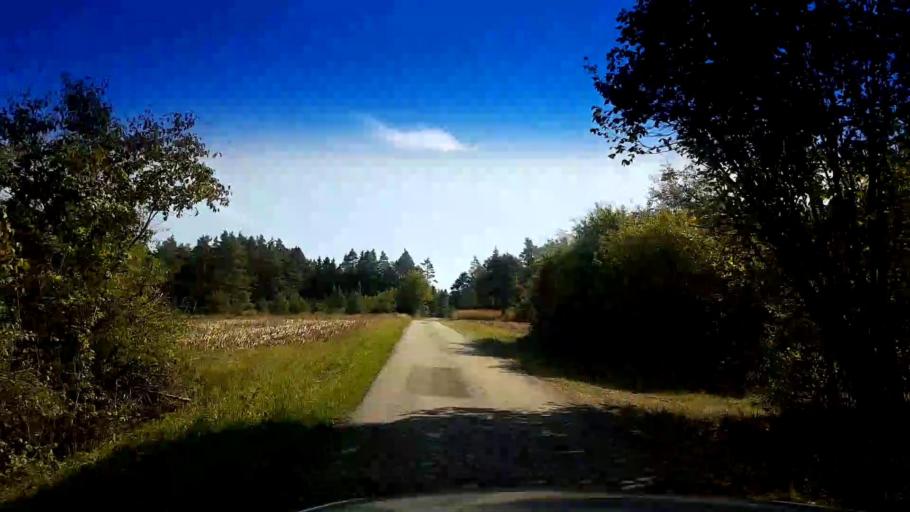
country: DE
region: Bavaria
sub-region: Upper Franconia
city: Poxdorf
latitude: 49.8822
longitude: 11.0882
